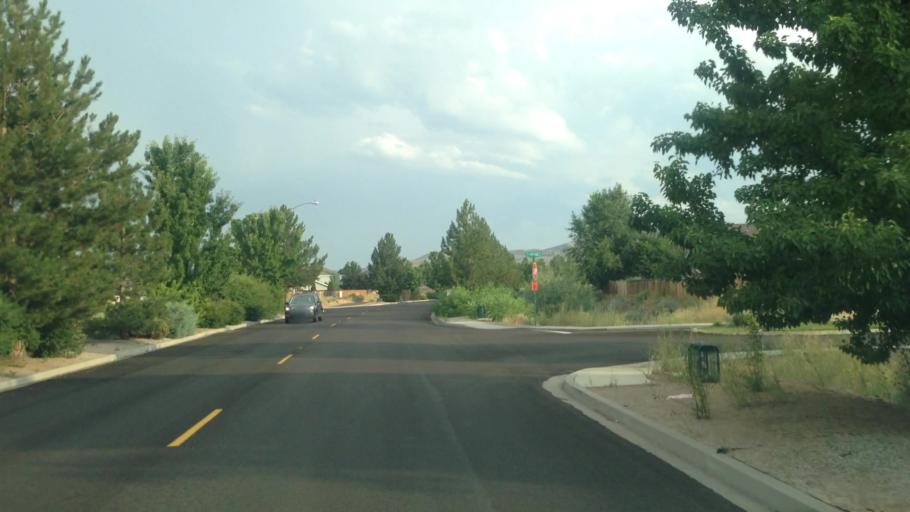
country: US
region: Nevada
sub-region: Washoe County
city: Lemmon Valley
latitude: 39.6297
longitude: -119.8755
